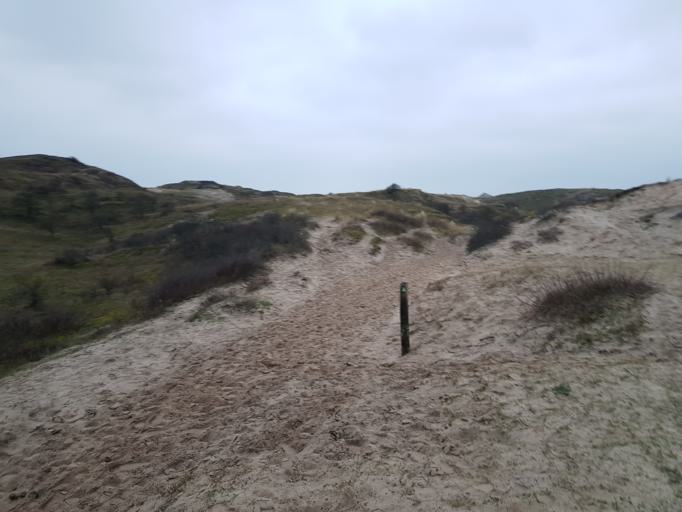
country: NL
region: North Holland
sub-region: Gemeente Bergen
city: Egmond aan Zee
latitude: 52.6324
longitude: 4.6337
